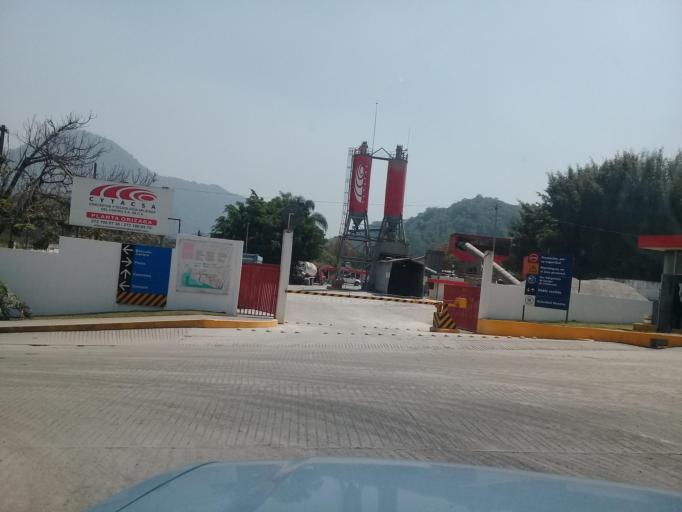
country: MX
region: Veracruz
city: Ixtac Zoquitlan
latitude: 18.8605
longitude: -97.0395
